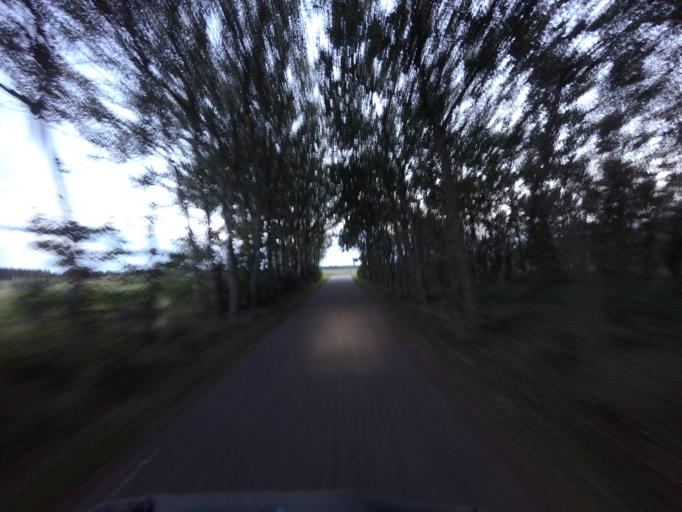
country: NL
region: Friesland
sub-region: Gemeente Ameland
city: Nes
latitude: 53.4525
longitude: 5.7977
